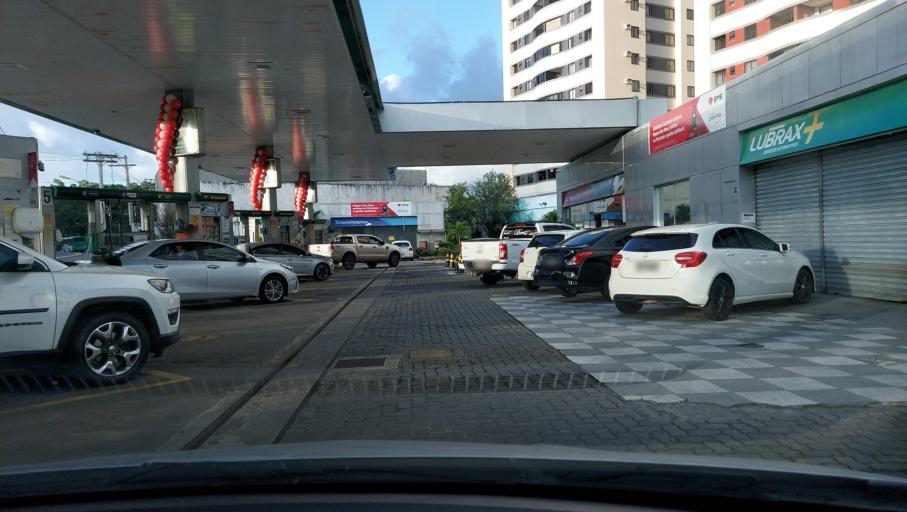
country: BR
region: Bahia
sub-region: Salvador
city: Salvador
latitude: -12.9818
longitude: -38.4499
